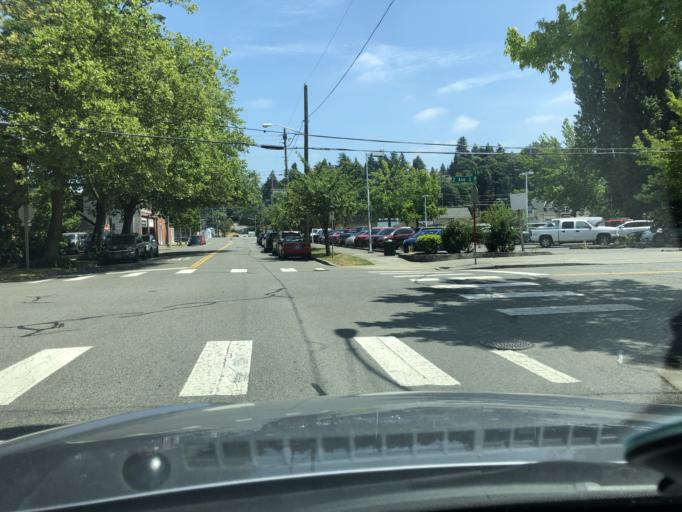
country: US
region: Washington
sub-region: King County
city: Kent
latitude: 47.3797
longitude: -122.2351
